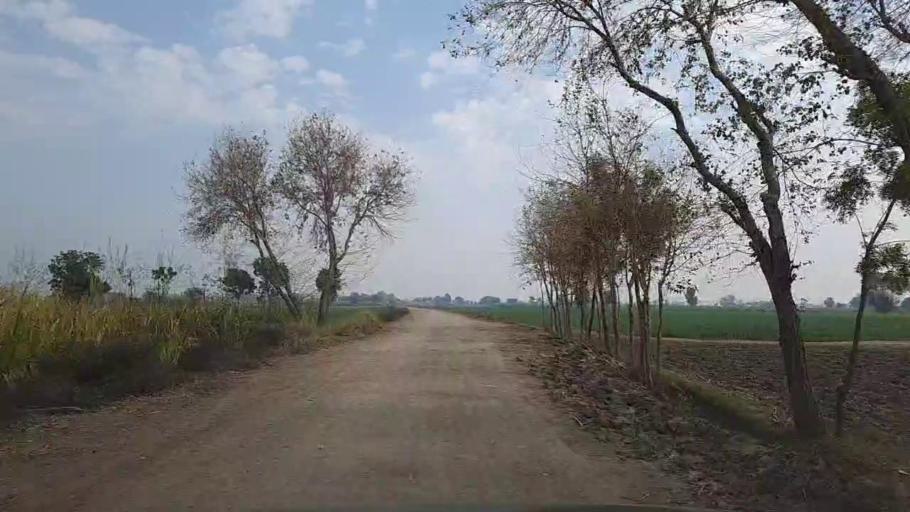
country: PK
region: Sindh
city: Daur
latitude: 26.3986
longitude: 68.3489
